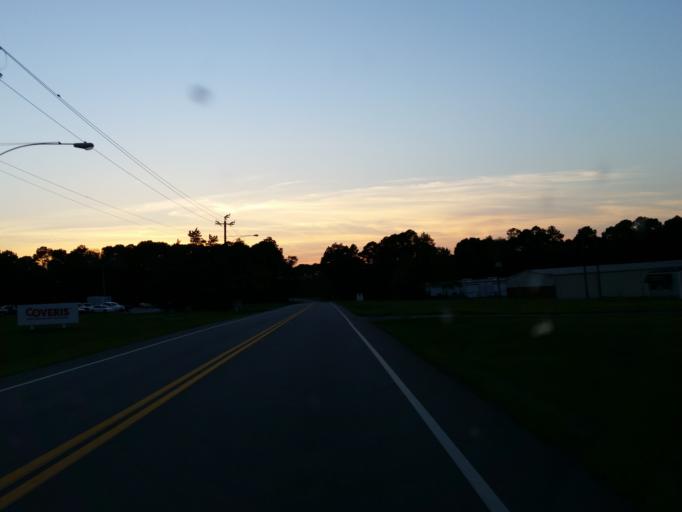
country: US
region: Georgia
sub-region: Tift County
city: Unionville
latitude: 31.4147
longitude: -83.4857
